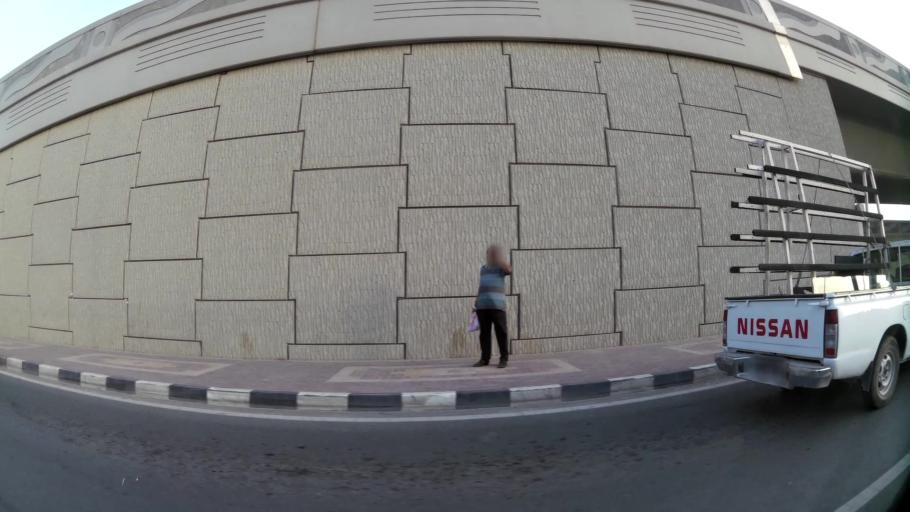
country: QA
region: Baladiyat ar Rayyan
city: Ar Rayyan
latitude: 25.2274
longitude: 51.4344
